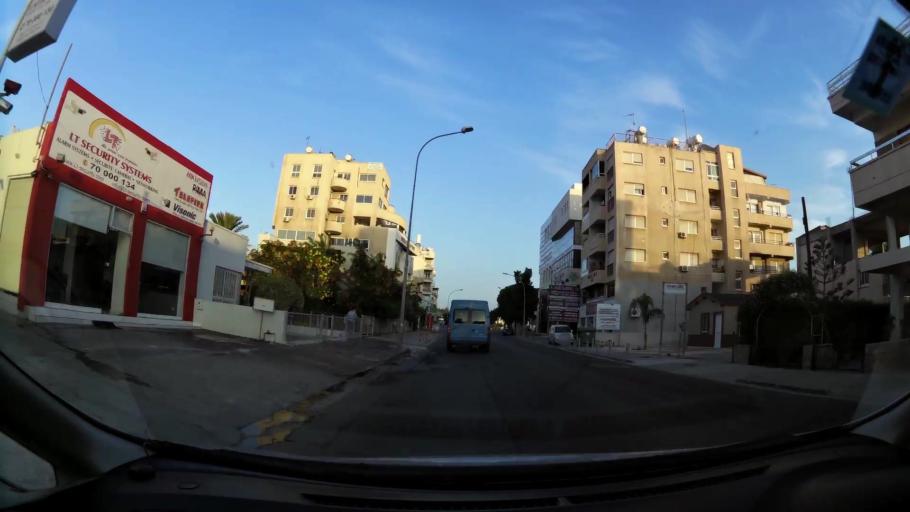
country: CY
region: Larnaka
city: Larnaca
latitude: 34.9216
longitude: 33.6141
